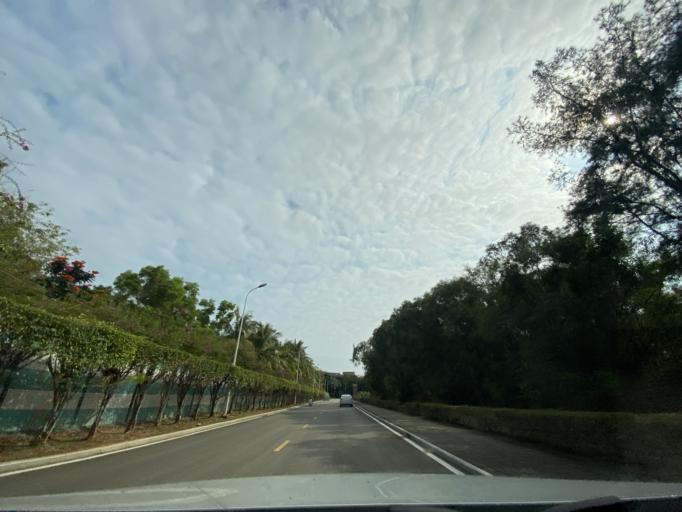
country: CN
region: Hainan
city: Tiandu
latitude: 18.2292
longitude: 109.6219
